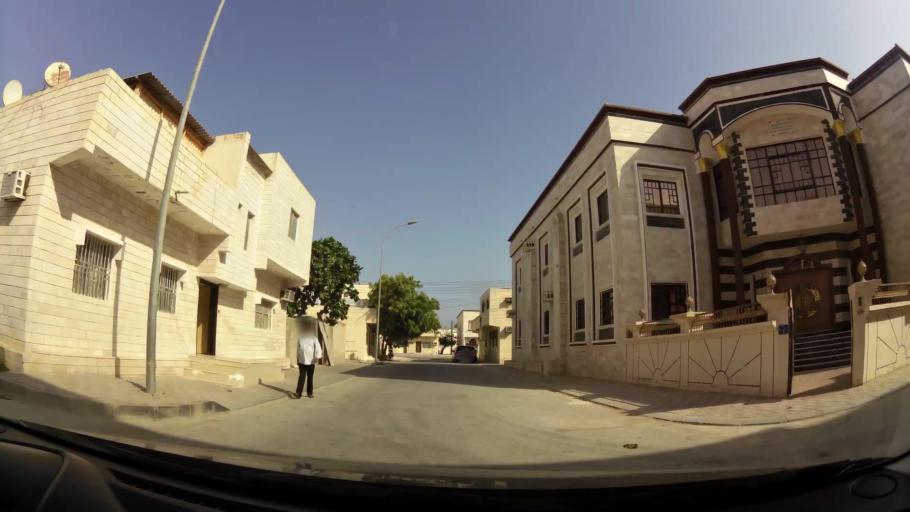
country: OM
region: Zufar
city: Salalah
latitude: 16.9998
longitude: 54.0372
